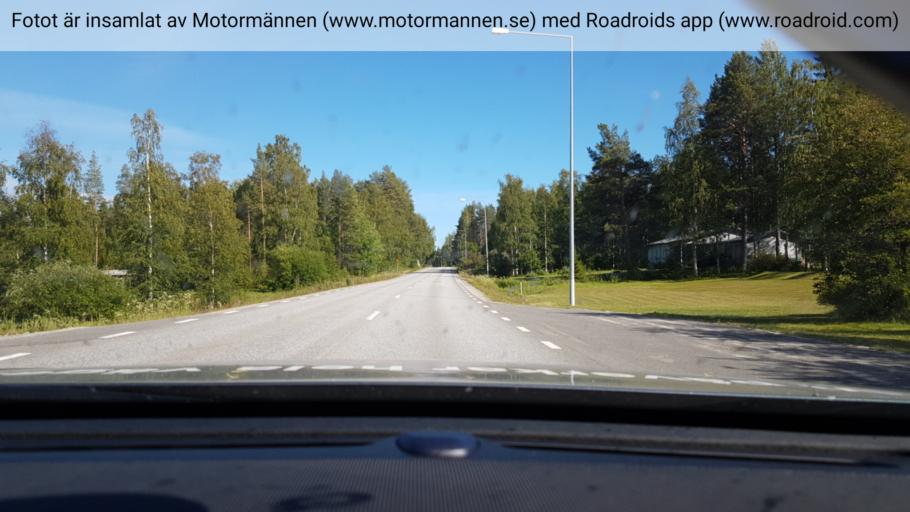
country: SE
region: Vaesterbotten
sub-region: Lycksele Kommun
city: Lycksele
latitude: 64.6376
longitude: 18.5324
